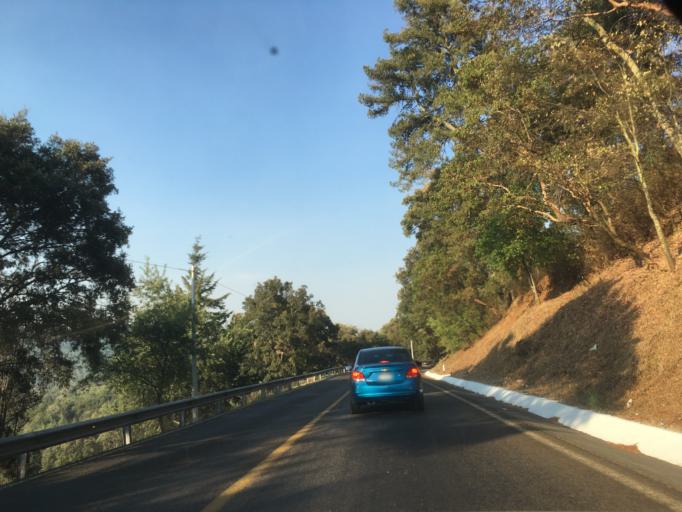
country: MX
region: Michoacan
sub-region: Morelia
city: Iratzio
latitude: 19.6280
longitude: -101.4573
